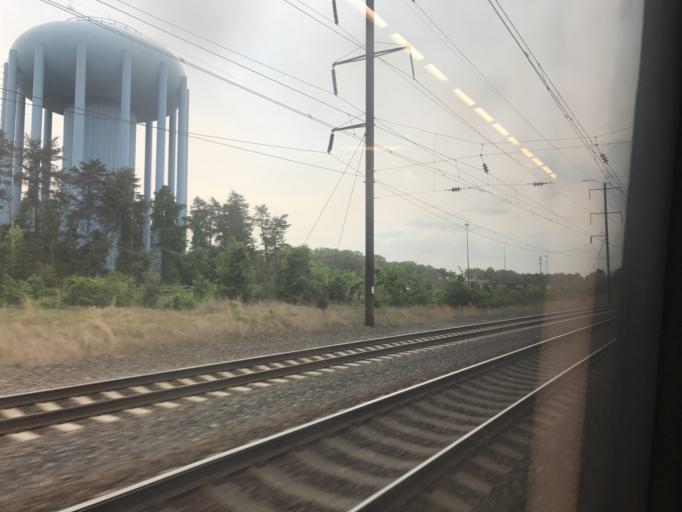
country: US
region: Maryland
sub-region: Anne Arundel County
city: Odenton
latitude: 39.0791
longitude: -76.7122
